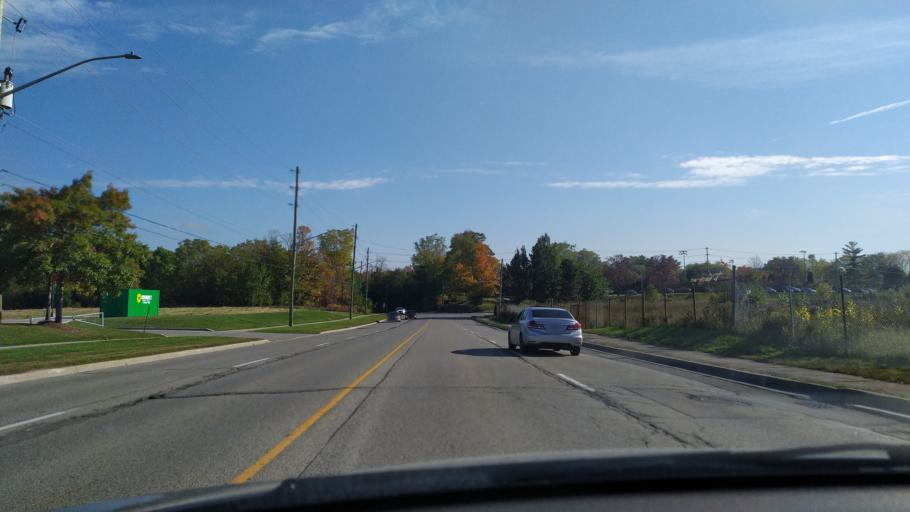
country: CA
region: Ontario
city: Waterloo
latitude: 43.4839
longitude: -80.5210
